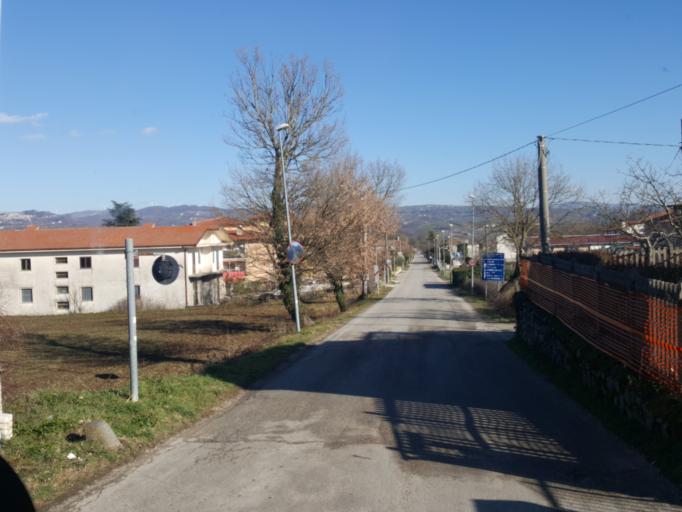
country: IT
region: Campania
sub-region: Provincia di Benevento
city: Morcone
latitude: 41.3424
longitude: 14.6771
